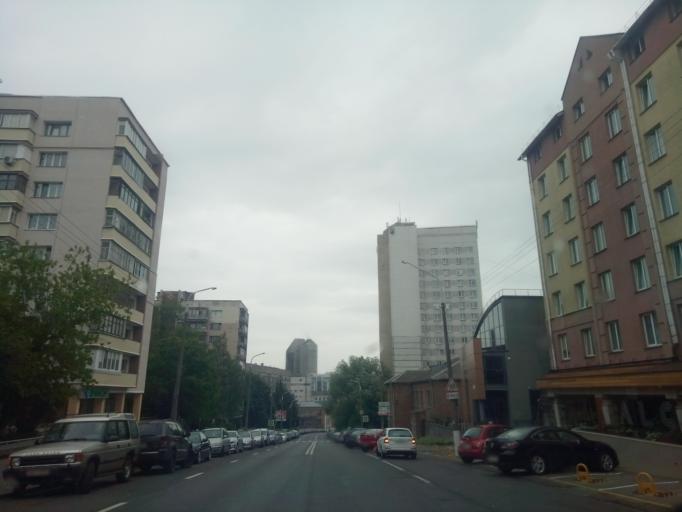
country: BY
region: Minsk
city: Minsk
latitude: 53.9023
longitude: 27.5424
